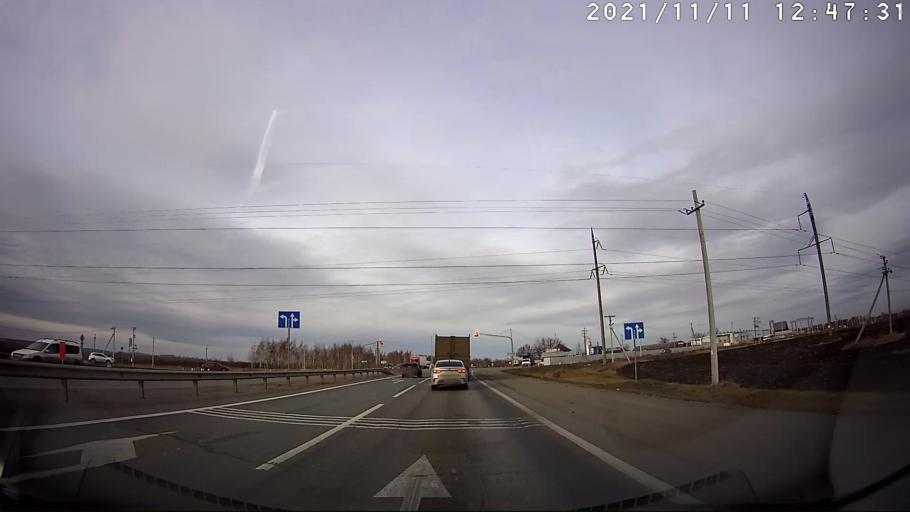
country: RU
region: Ulyanovsk
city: Novoul'yanovsk
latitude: 54.2289
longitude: 48.2542
